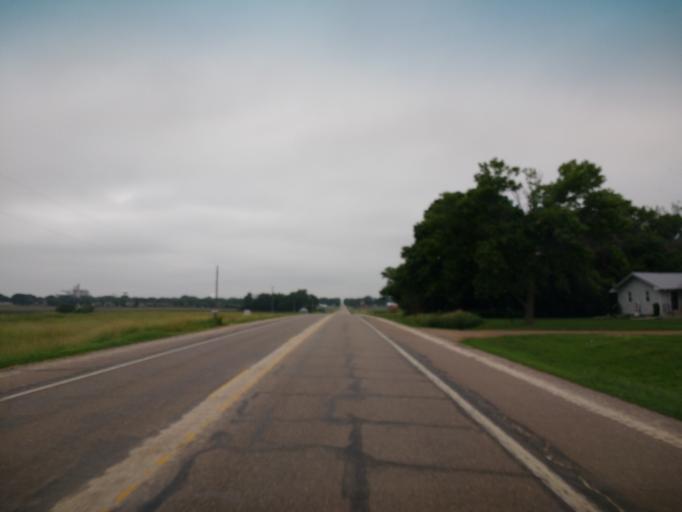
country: US
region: Iowa
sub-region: O'Brien County
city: Hartley
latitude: 43.1847
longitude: -95.4528
